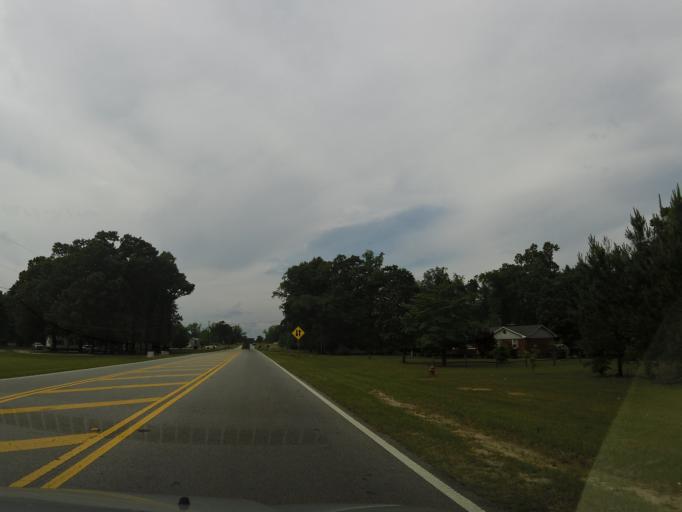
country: US
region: Georgia
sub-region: Jefferson County
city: Wrens
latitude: 33.2204
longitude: -82.3996
